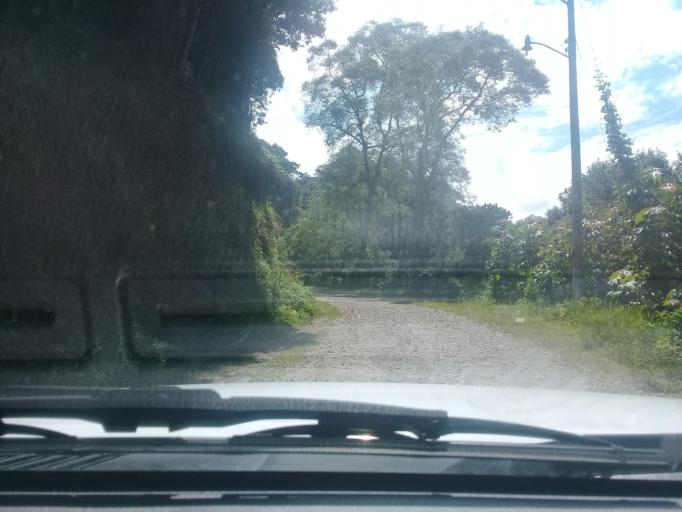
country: MX
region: Veracruz
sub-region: Tlalnelhuayocan
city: Otilpan
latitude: 19.5667
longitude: -96.9798
